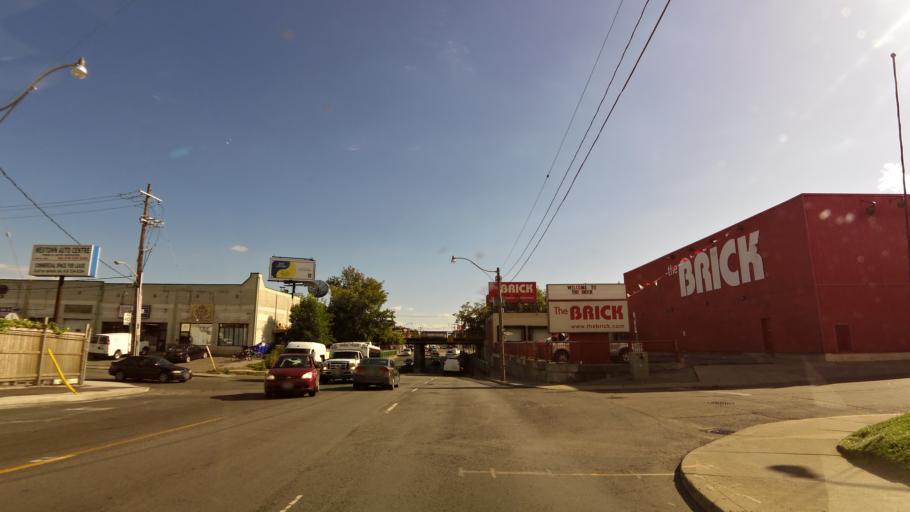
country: CA
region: Ontario
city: Toronto
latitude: 43.6696
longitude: -79.4396
